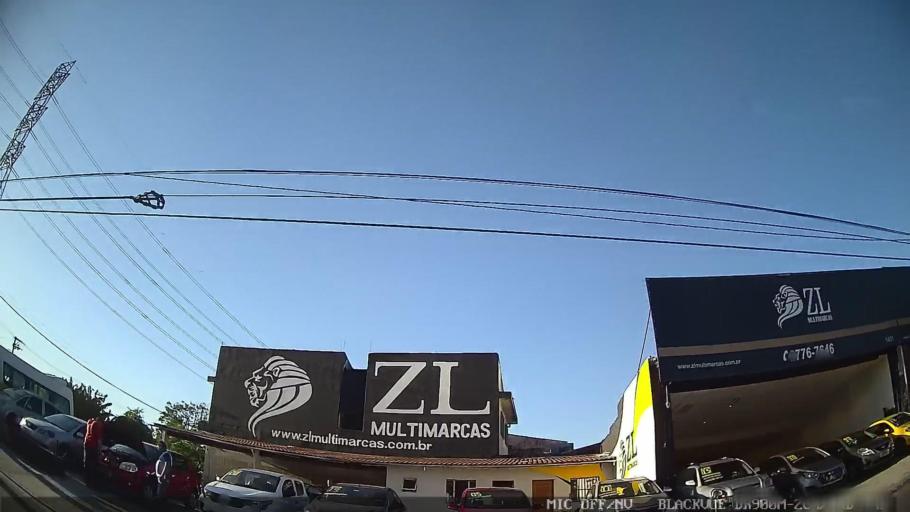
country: BR
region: Sao Paulo
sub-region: Sao Caetano Do Sul
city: Sao Caetano do Sul
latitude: -23.5503
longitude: -46.5108
